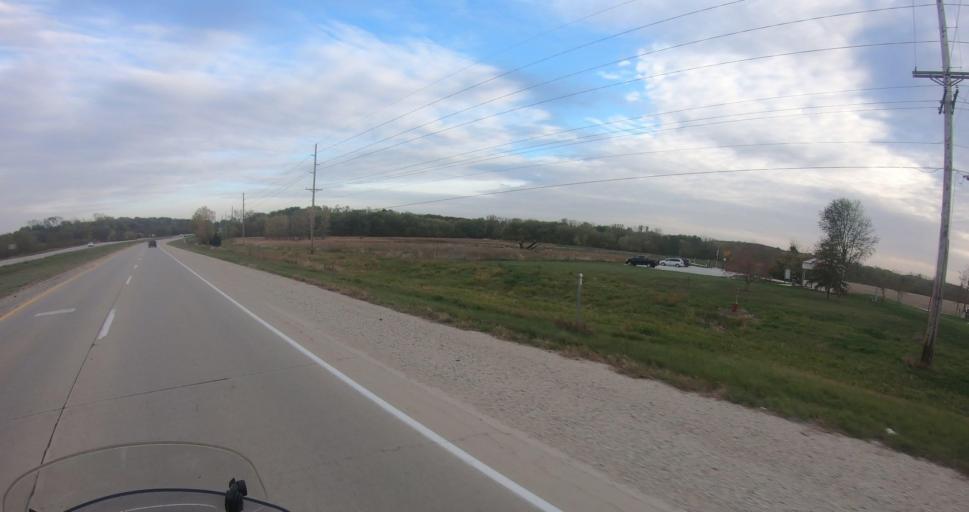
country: US
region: Iowa
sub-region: Warren County
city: Carlisle
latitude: 41.5080
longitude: -93.5146
